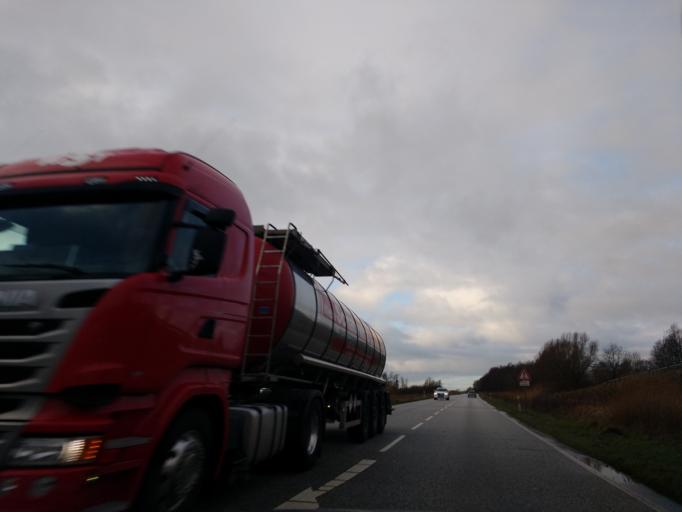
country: DE
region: Schleswig-Holstein
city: Heiligenstedten
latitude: 53.9364
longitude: 9.4697
